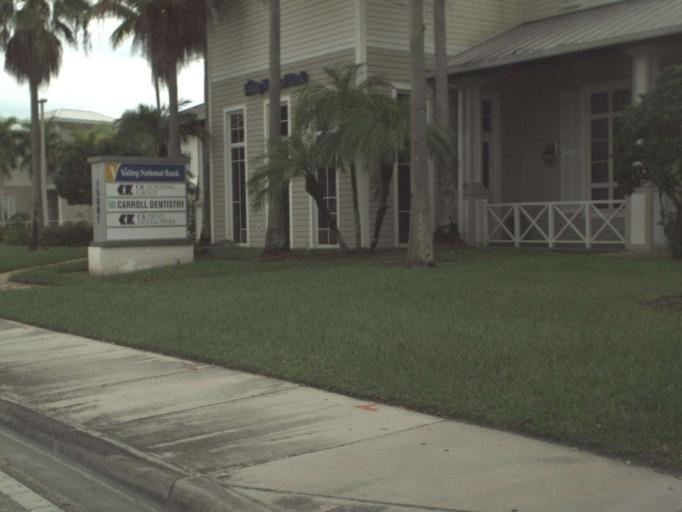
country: US
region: Florida
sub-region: Miami-Dade County
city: North Miami Beach
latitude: 25.9208
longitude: -80.1552
